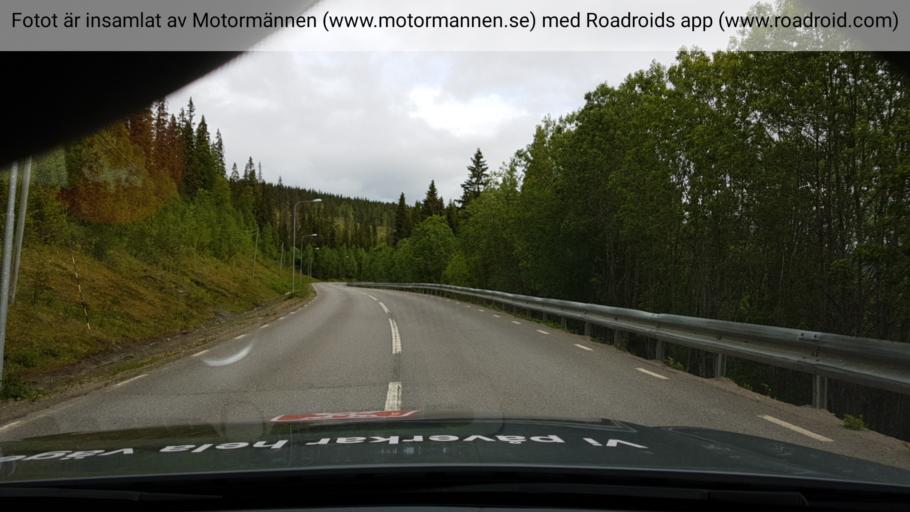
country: NO
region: Nord-Trondelag
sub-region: Lierne
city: Sandvika
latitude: 64.4875
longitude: 14.1357
